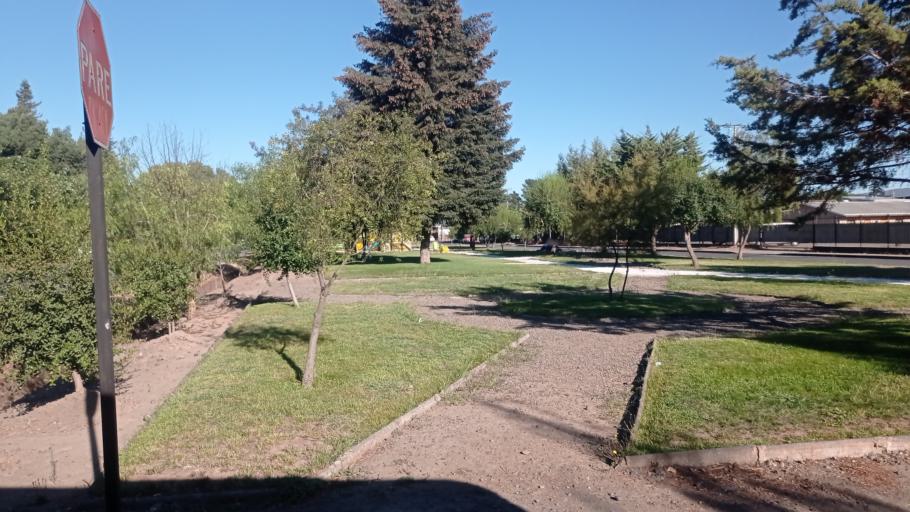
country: CL
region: Biobio
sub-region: Provincia de Biobio
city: Nacimiento
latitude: -37.5102
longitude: -72.6595
